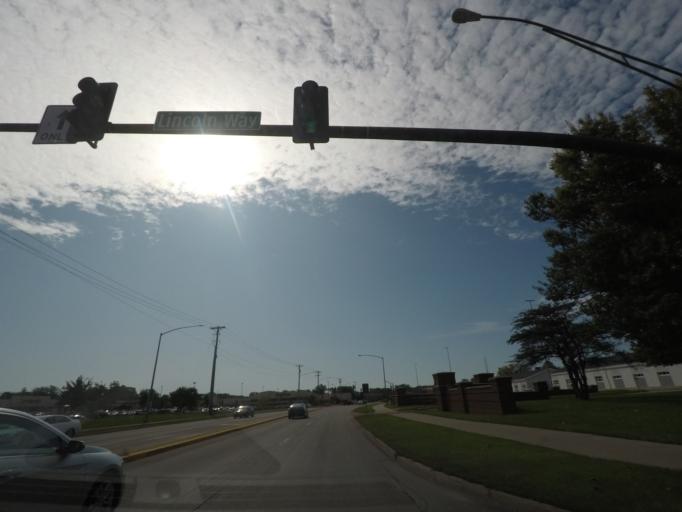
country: US
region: Iowa
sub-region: Story County
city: Ames
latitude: 42.0226
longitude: -93.6203
